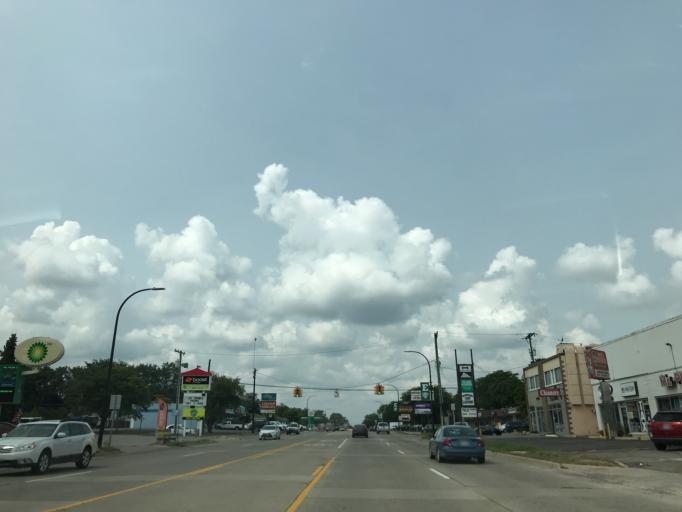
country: US
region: Michigan
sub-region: Washtenaw County
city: Ypsilanti
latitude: 42.2472
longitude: -83.6359
